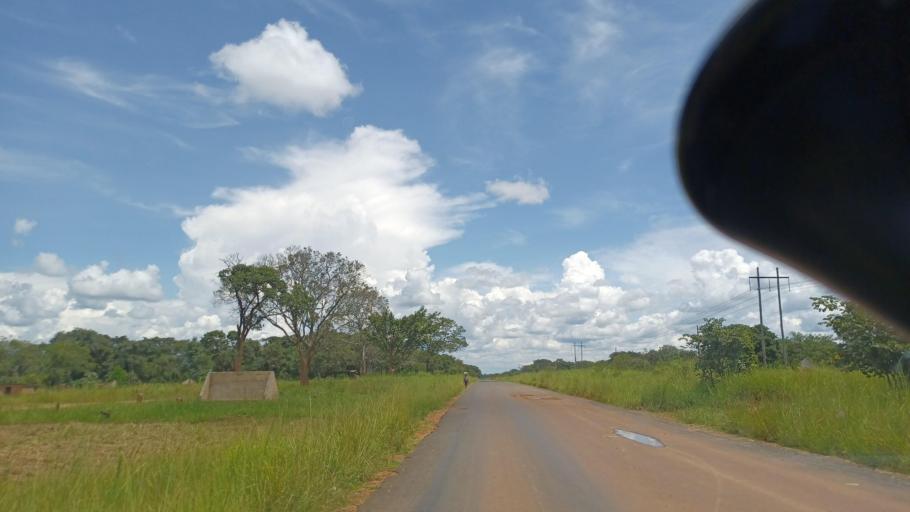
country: ZM
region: North-Western
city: Solwezi
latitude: -12.5651
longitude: 26.1389
